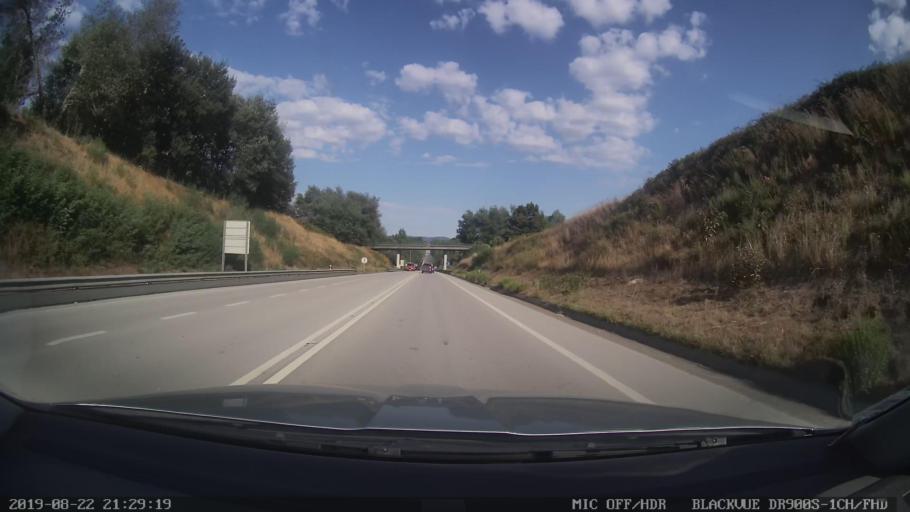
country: PT
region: Leiria
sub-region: Pedrogao Grande
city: Pedrogao Grande
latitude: 39.9013
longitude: -8.1332
